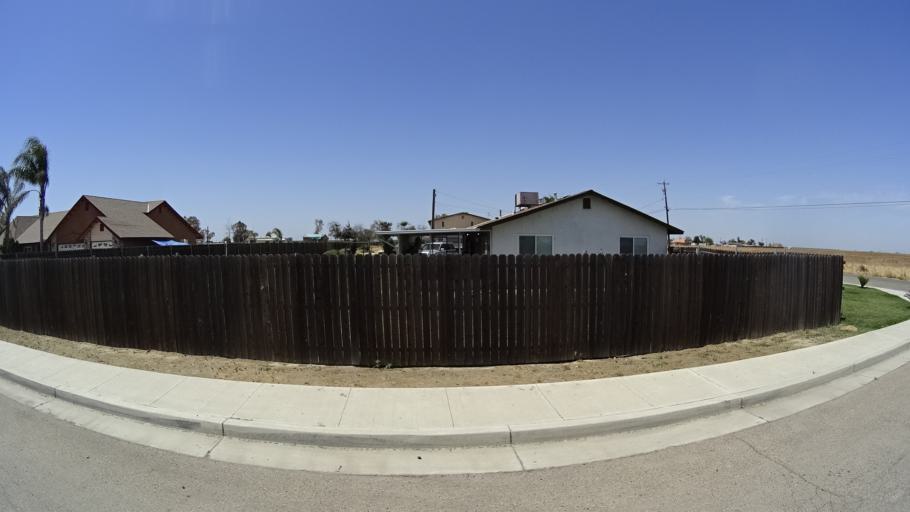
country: US
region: California
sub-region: Kings County
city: Corcoran
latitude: 36.1160
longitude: -119.5722
